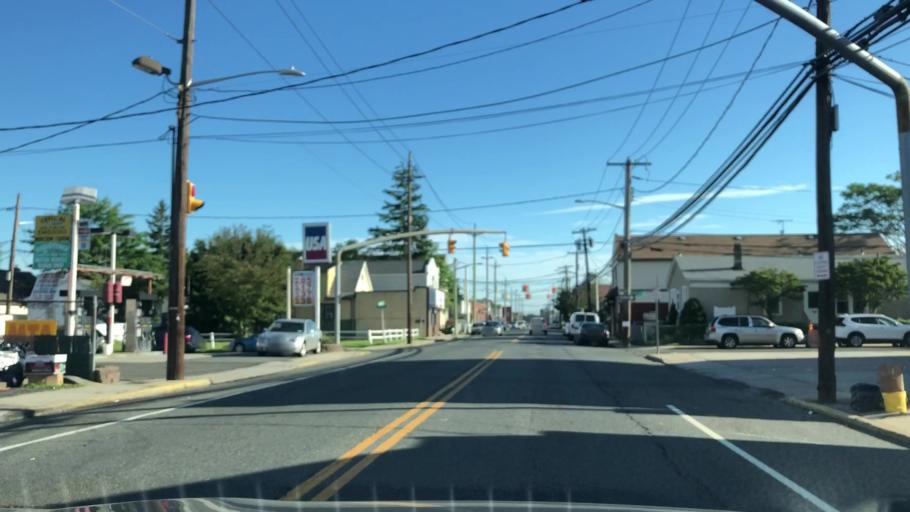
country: US
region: New York
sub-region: Nassau County
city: Franklin Square
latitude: 40.6998
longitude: -73.6907
